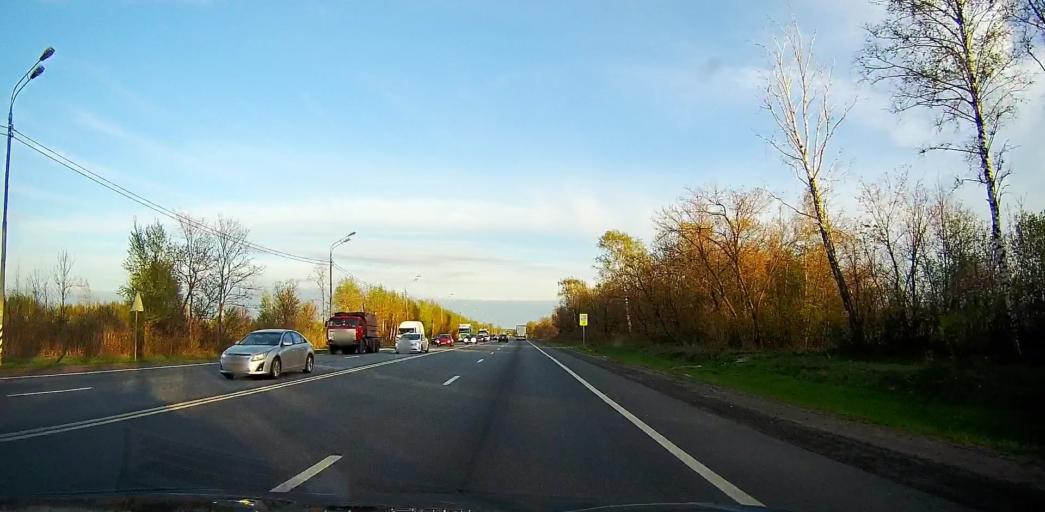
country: RU
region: Moskovskaya
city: Troitskoye
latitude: 55.2690
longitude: 38.5009
